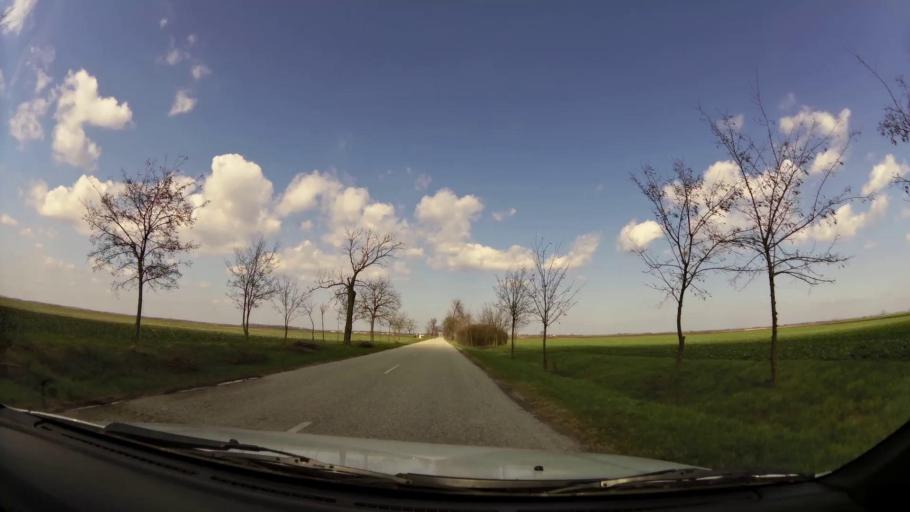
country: HU
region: Pest
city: Tapiogyorgye
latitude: 47.3054
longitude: 19.9410
